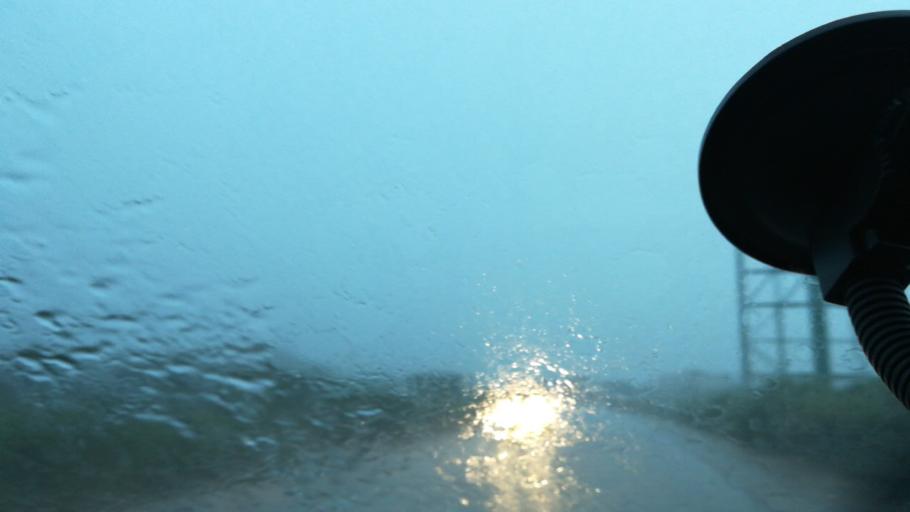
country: CD
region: Katanga
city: Lubumbashi
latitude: -11.5934
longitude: 27.4982
